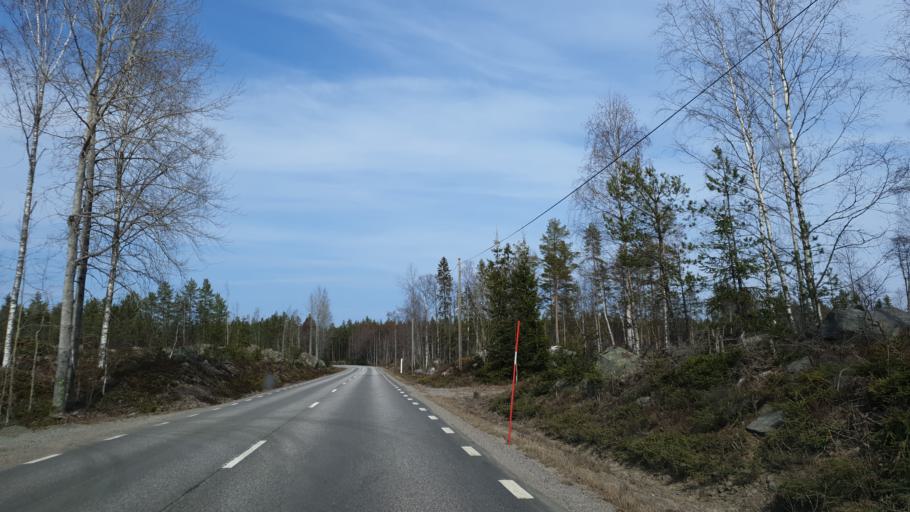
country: SE
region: Gaevleborg
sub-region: Gavle Kommun
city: Norrsundet
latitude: 61.0215
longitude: 17.1461
